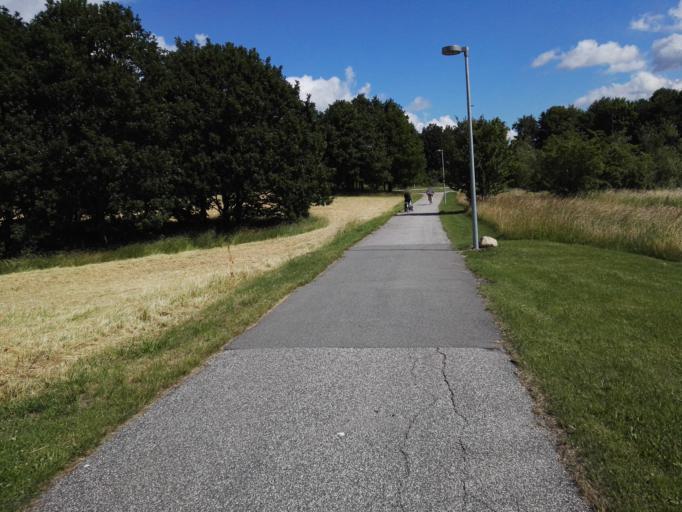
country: DK
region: Capital Region
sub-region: Ballerup Kommune
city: Ballerup
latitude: 55.7414
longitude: 12.3898
